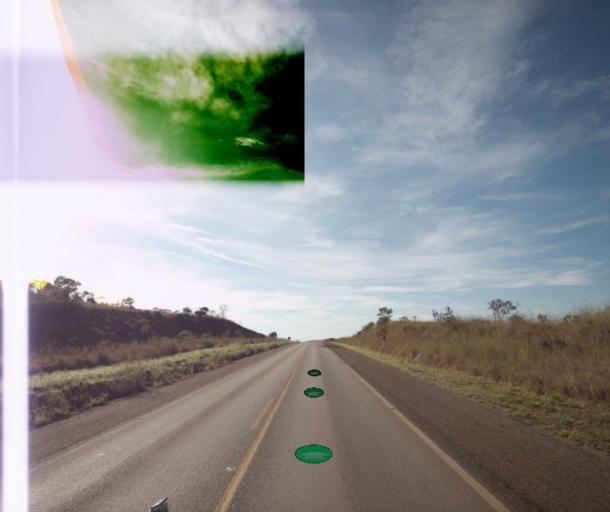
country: BR
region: Goias
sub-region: Abadiania
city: Abadiania
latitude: -15.7842
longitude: -48.4850
